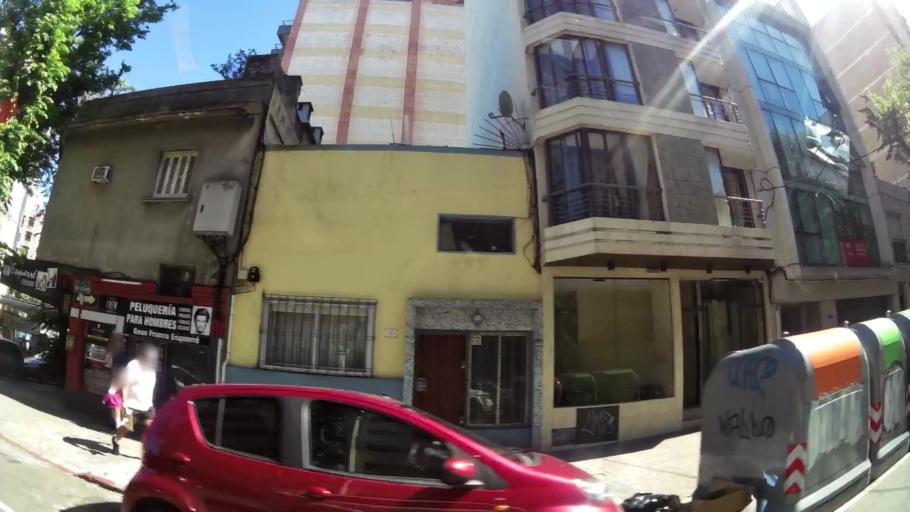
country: UY
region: Montevideo
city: Montevideo
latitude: -34.8990
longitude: -56.1668
